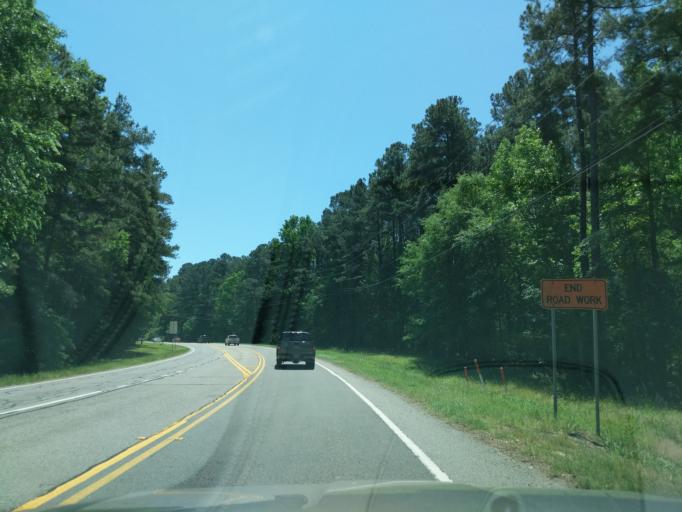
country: US
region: Georgia
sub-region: Columbia County
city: Evans
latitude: 33.5681
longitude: -82.1158
